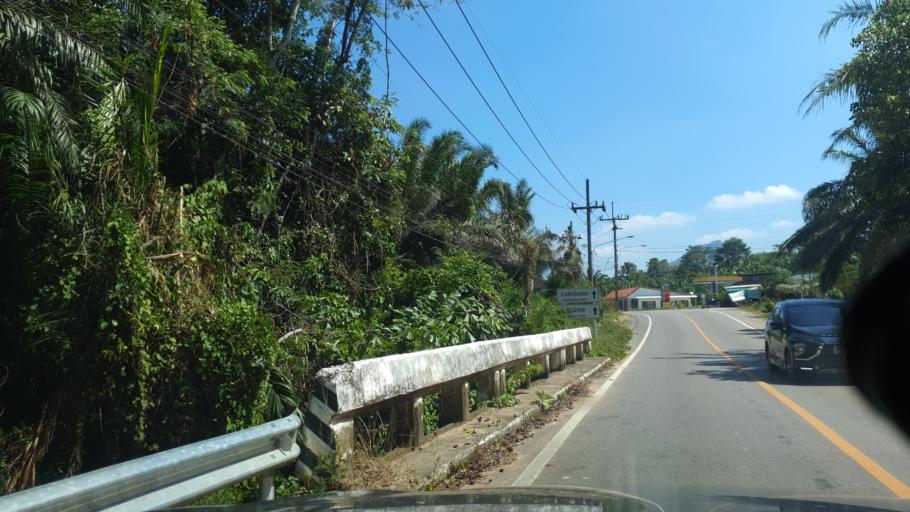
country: TH
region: Krabi
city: Khlong Thom
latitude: 7.9207
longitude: 99.2522
